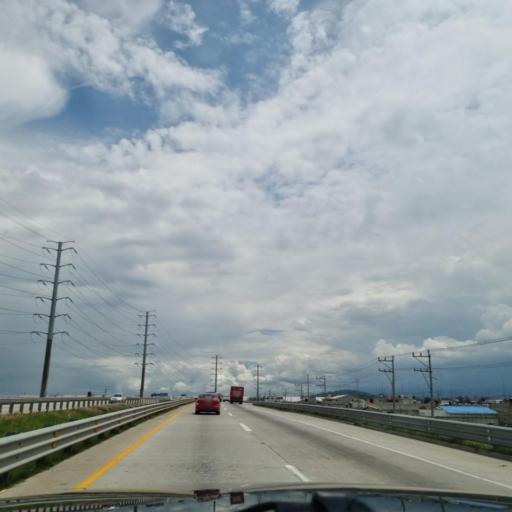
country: MX
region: Puebla
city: Moyotzingo
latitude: 19.2759
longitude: -98.4115
